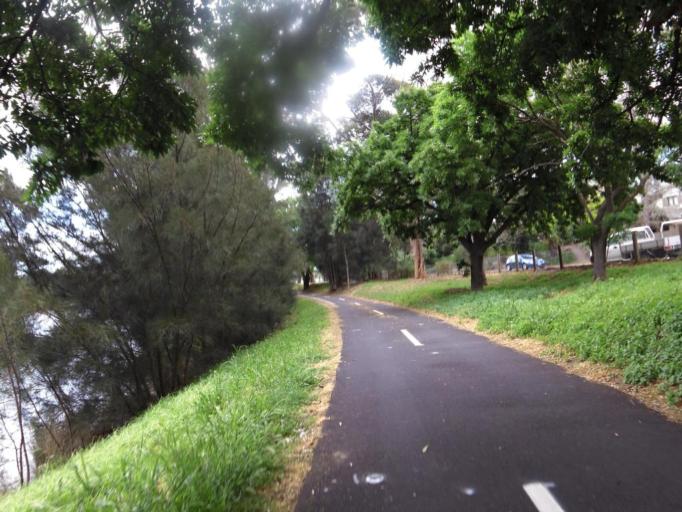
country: AU
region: Victoria
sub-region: Stonnington
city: Toorak
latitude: -37.8333
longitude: 145.0105
